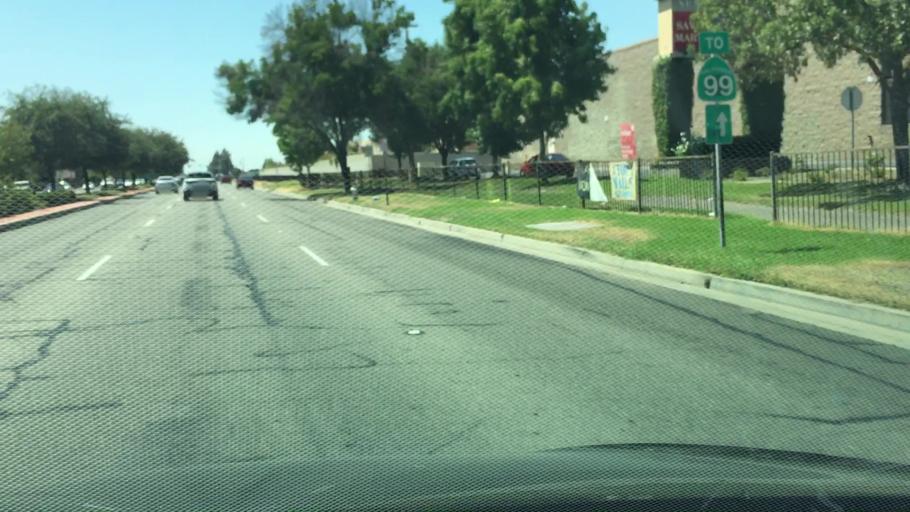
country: US
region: California
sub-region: Fresno County
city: Fresno
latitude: 36.8374
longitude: -119.8488
